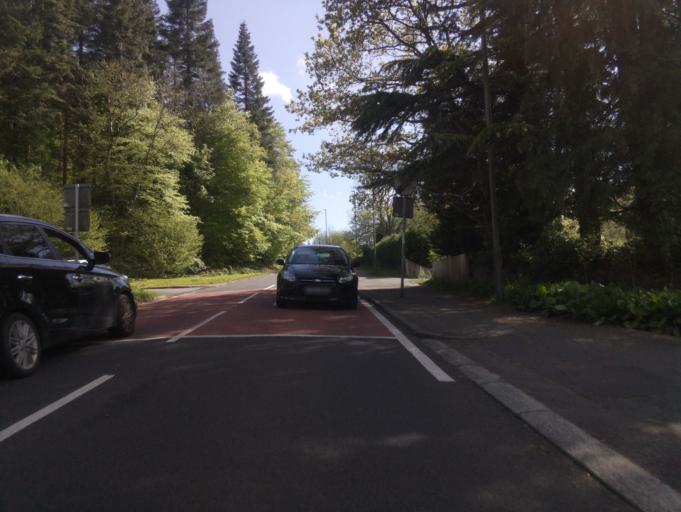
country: GB
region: Wales
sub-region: Caerphilly County Borough
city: Caerphilly
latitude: 51.5663
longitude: -3.2168
